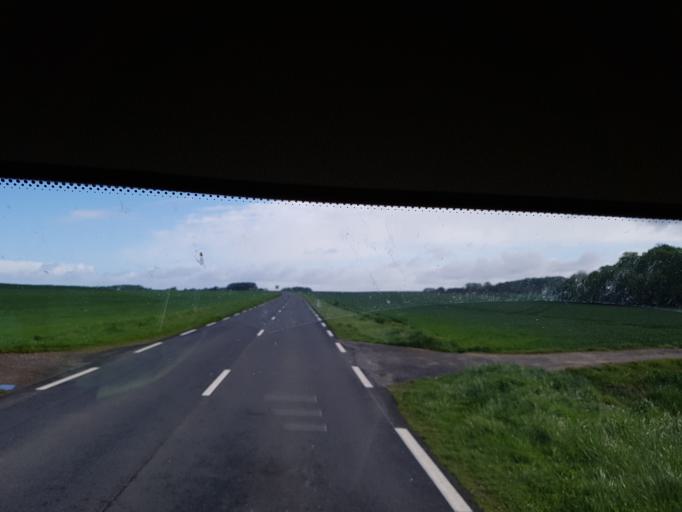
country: FR
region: Picardie
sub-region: Departement de l'Aisne
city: Sinceny
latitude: 49.5924
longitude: 3.2667
